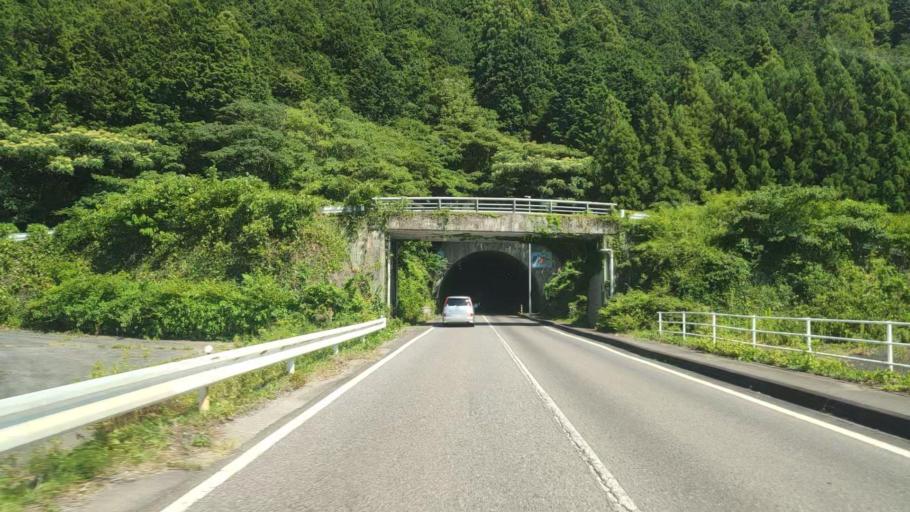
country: JP
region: Gifu
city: Godo
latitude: 35.5156
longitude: 136.6545
